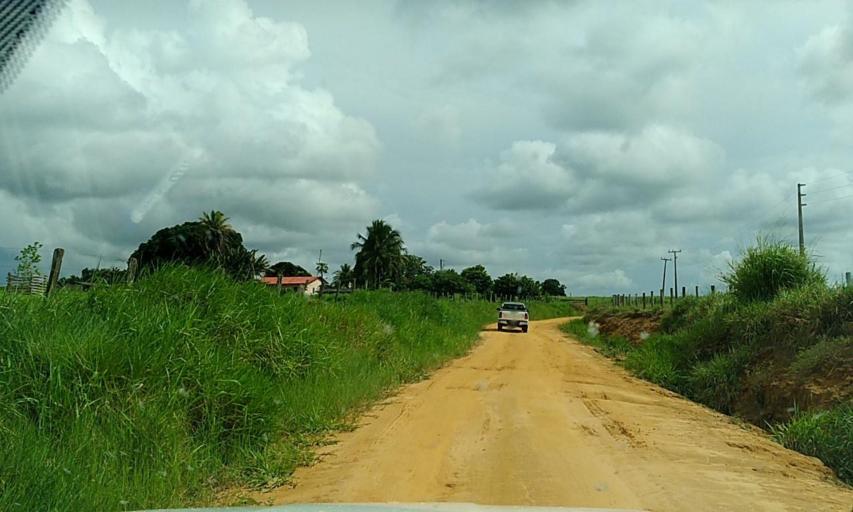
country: BR
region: Para
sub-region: Altamira
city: Altamira
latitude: -3.2523
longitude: -52.6940
